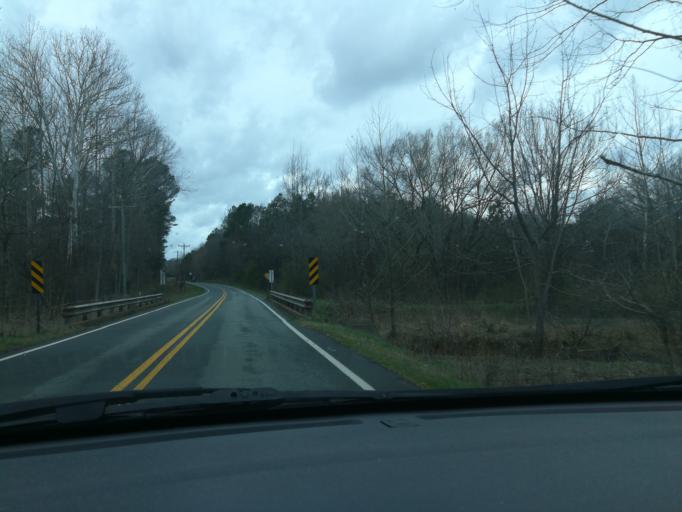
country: US
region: North Carolina
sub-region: Orange County
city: Hillsborough
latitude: 36.0344
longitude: -79.0473
